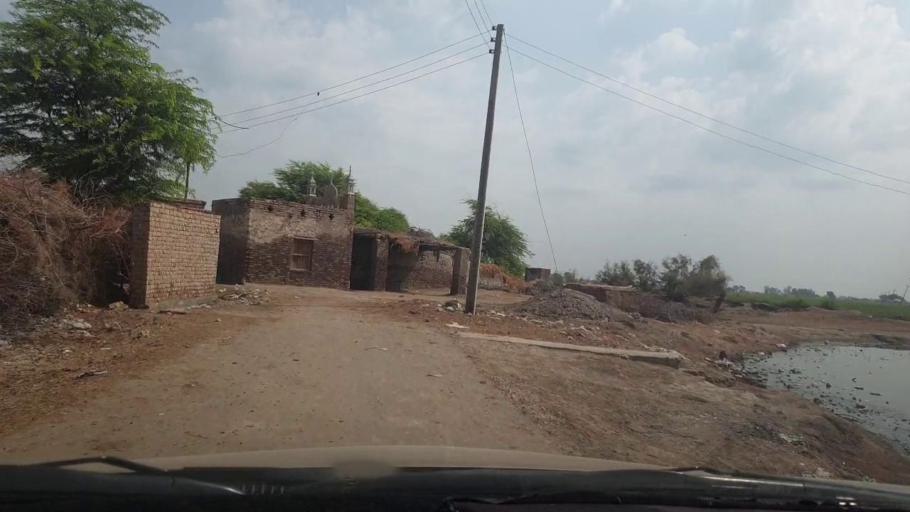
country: PK
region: Sindh
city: Larkana
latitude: 27.6651
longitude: 68.1819
